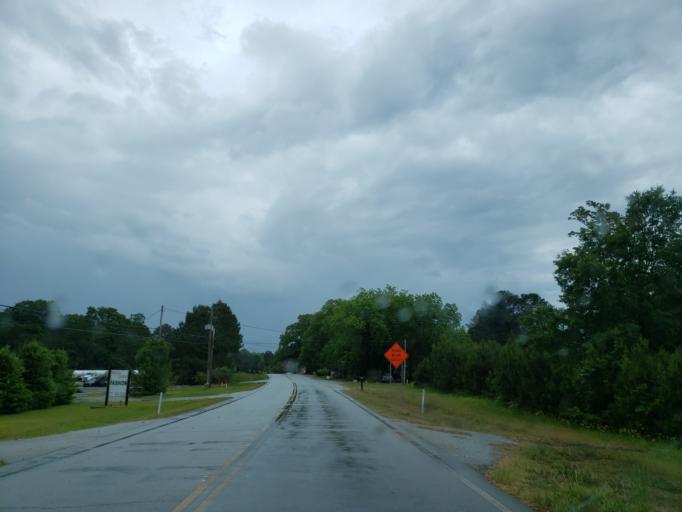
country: US
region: Georgia
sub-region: Haralson County
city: Buchanan
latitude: 33.7899
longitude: -85.1803
